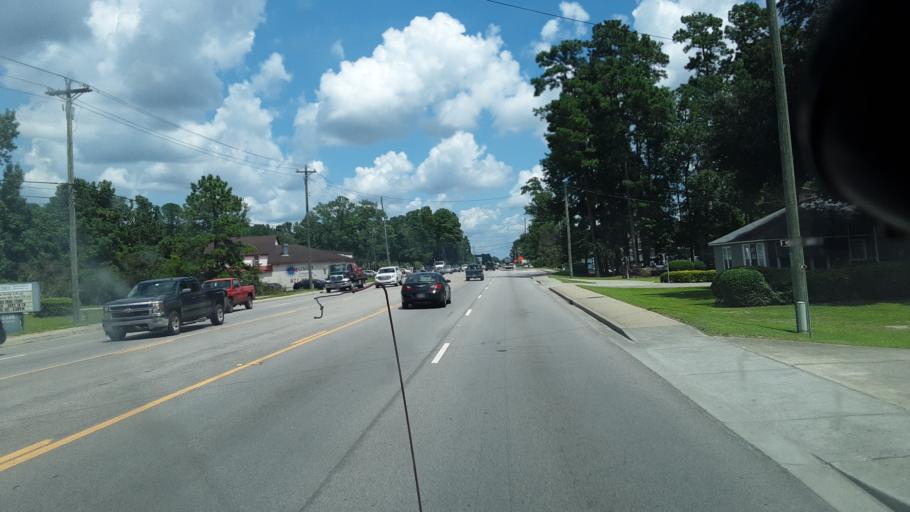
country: US
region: South Carolina
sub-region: Berkeley County
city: Sangaree
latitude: 33.0499
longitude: -80.1045
